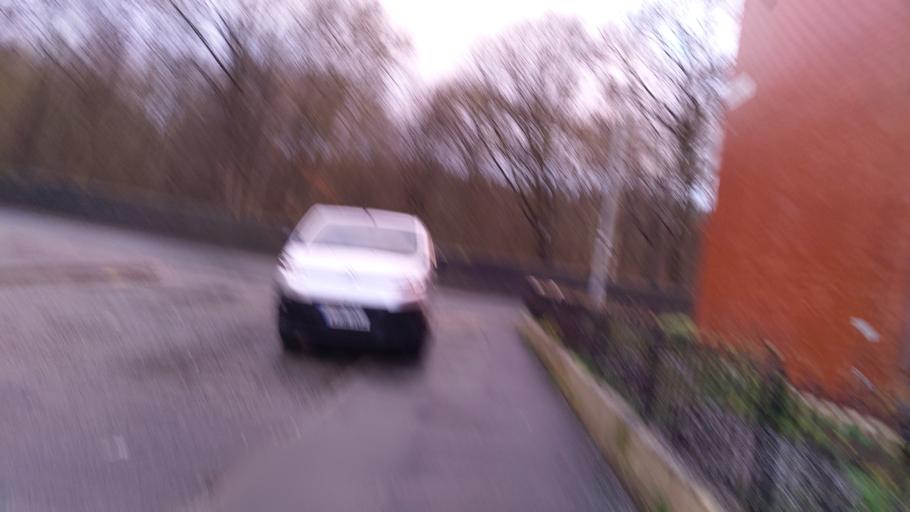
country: GB
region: England
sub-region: Blackburn with Darwen
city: Blackburn
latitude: 53.7390
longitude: -2.5103
